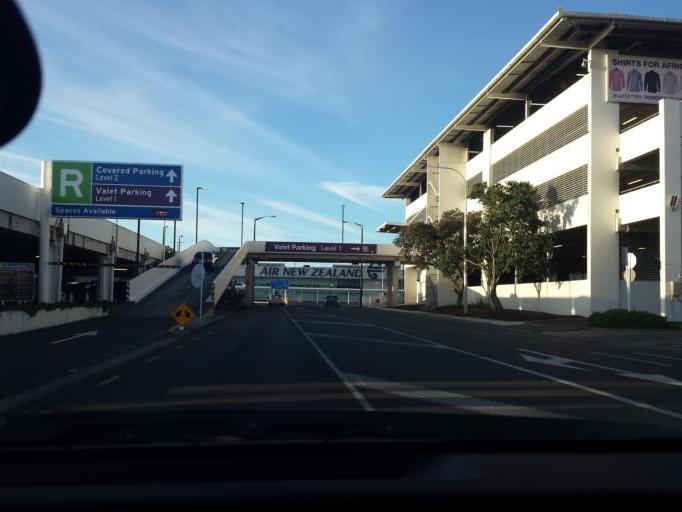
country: NZ
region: Auckland
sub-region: Auckland
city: Mangere
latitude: -37.0051
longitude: 174.7908
